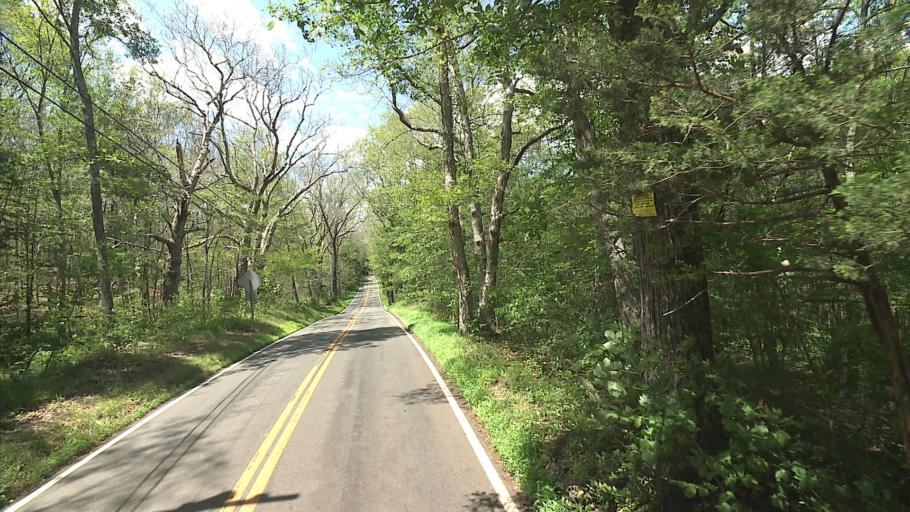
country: US
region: Connecticut
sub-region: Middlesex County
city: Essex Village
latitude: 41.4458
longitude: -72.3367
